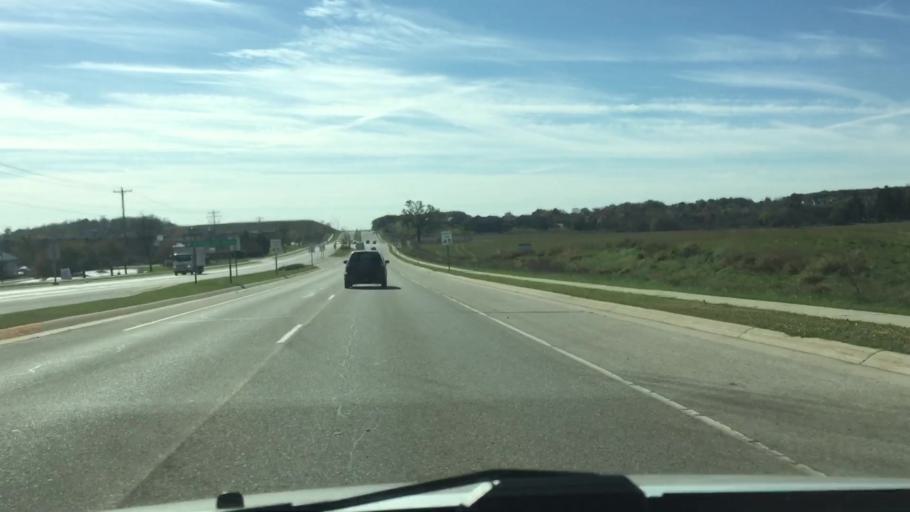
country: US
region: Wisconsin
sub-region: Waukesha County
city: Sussex
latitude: 43.1171
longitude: -88.2446
